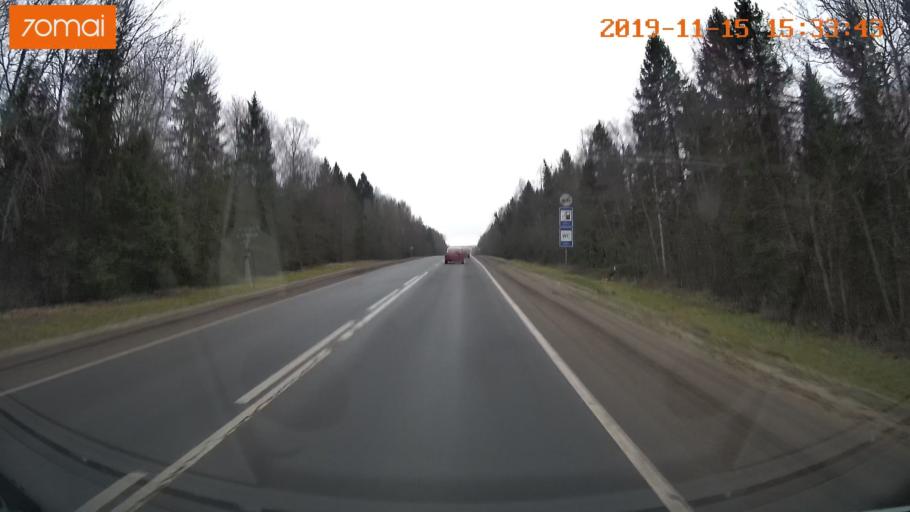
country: RU
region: Jaroslavl
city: Danilov
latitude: 58.0775
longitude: 40.0916
